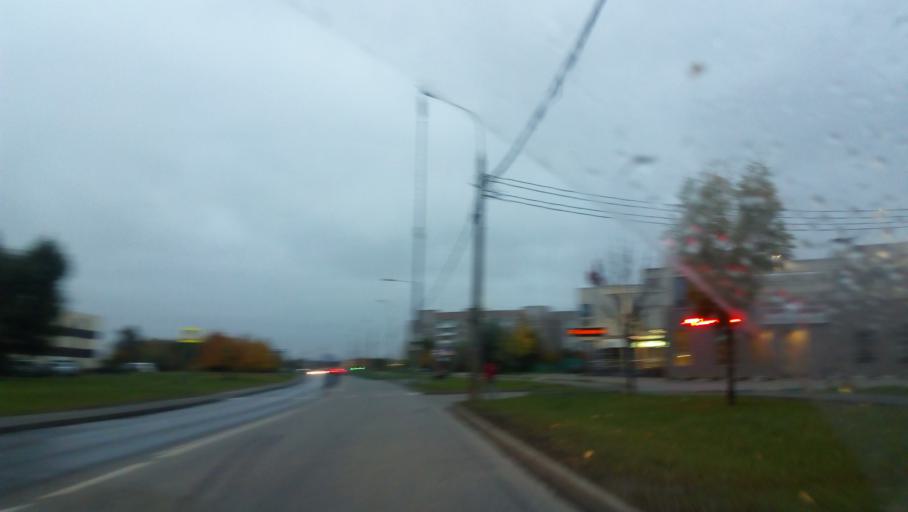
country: RU
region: Moskovskaya
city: Reutov
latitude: 55.7342
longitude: 37.8629
